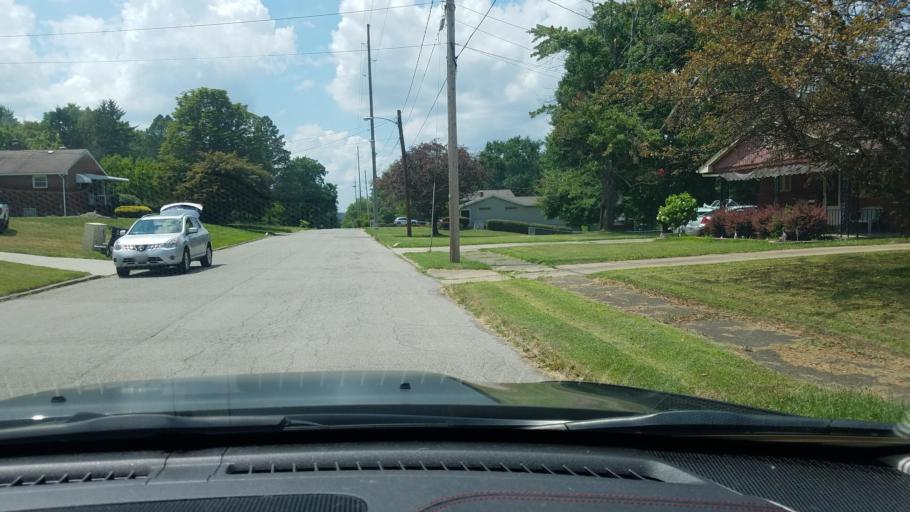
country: US
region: Ohio
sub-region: Mahoning County
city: Campbell
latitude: 41.0786
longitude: -80.5812
